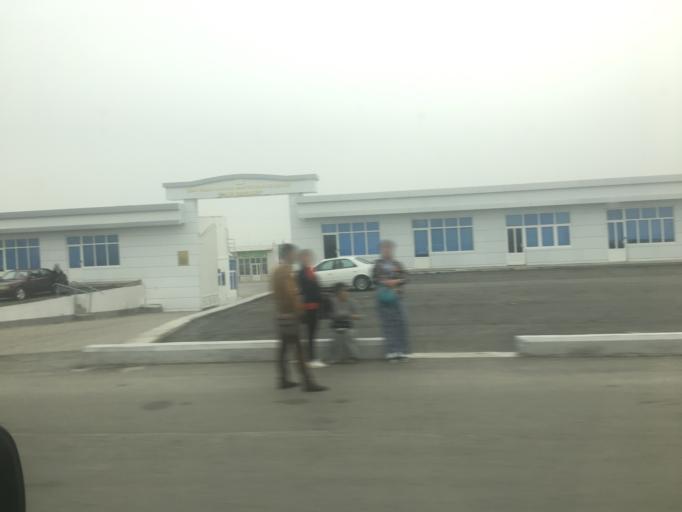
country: TM
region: Lebap
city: Turkmenabat
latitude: 38.9925
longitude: 63.5818
